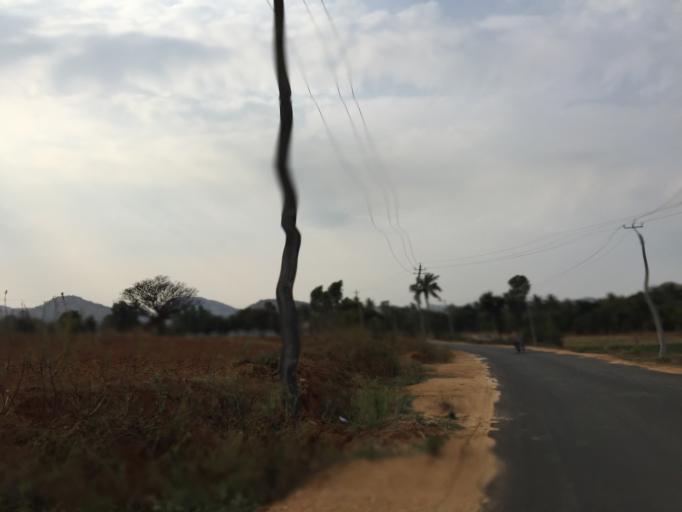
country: IN
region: Karnataka
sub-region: Chikkaballapur
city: Gudibanda
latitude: 13.5712
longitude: 77.7292
